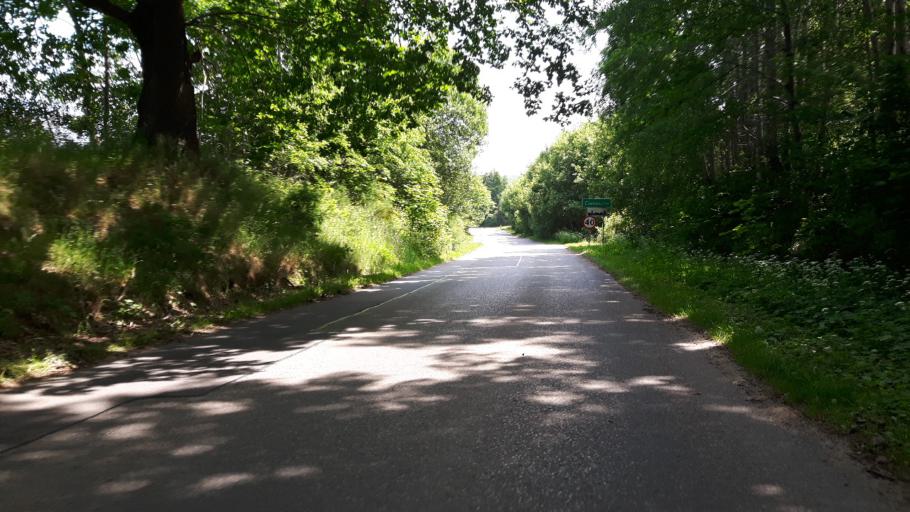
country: PL
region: Pomeranian Voivodeship
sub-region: Powiat wejherowski
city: Choczewo
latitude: 54.7568
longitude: 17.7819
